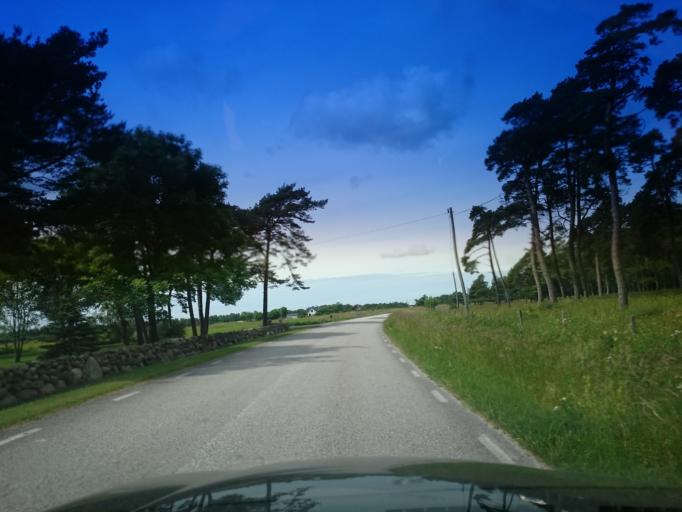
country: SE
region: Gotland
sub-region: Gotland
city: Hemse
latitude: 57.2545
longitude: 18.6077
